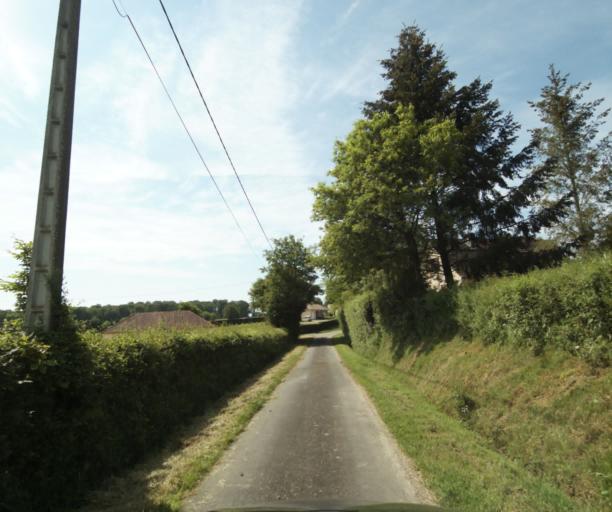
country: FR
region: Bourgogne
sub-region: Departement de Saone-et-Loire
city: Palinges
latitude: 46.5544
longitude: 4.1793
